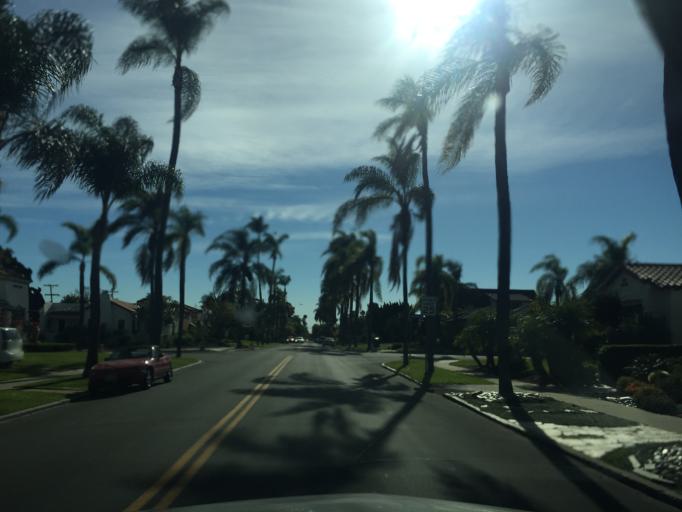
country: US
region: California
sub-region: San Diego County
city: San Diego
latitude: 32.7672
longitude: -117.1063
